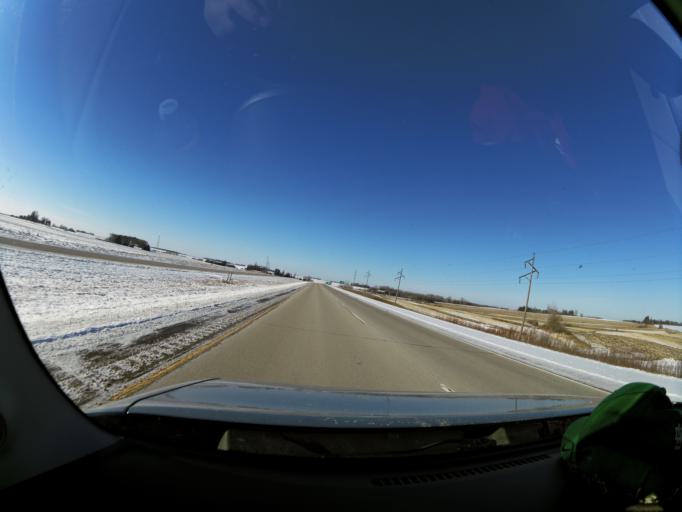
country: US
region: Minnesota
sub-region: Goodhue County
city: Wanamingo
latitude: 44.3606
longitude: -92.7918
